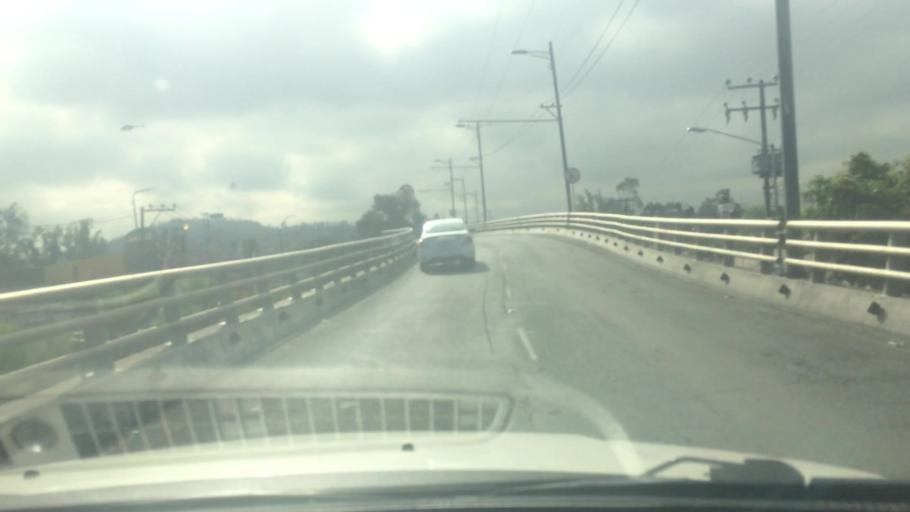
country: MX
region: Mexico City
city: Coyoacan
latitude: 19.3392
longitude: -99.1157
